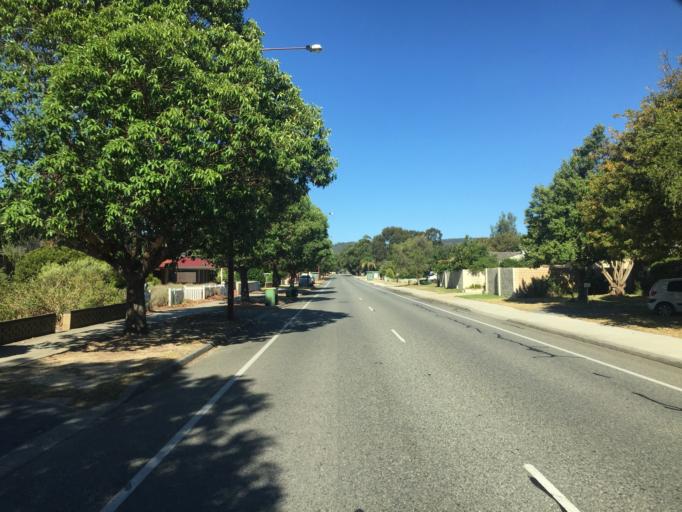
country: AU
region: Western Australia
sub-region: Gosnells
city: Gosnells
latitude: -32.0629
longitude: 116.0022
